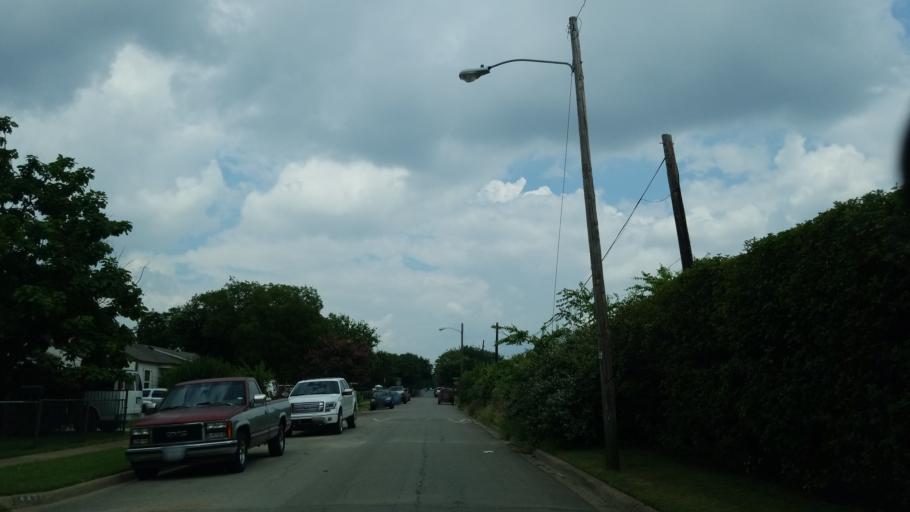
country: US
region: Texas
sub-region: Dallas County
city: University Park
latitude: 32.8477
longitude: -96.8347
